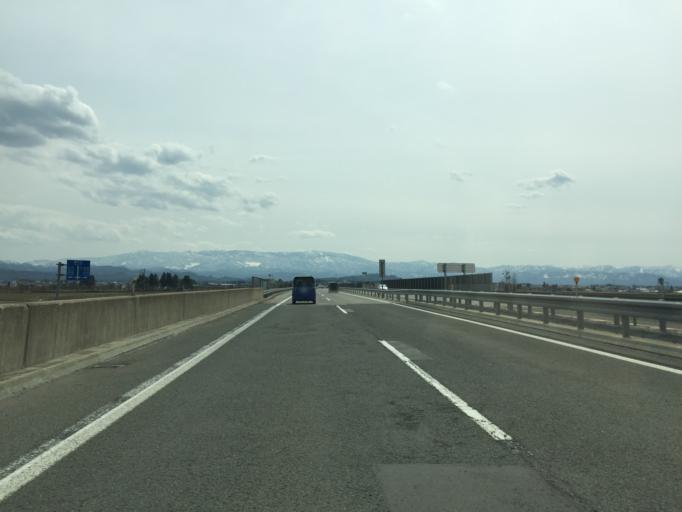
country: JP
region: Yamagata
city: Takahata
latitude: 38.0069
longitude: 140.1568
